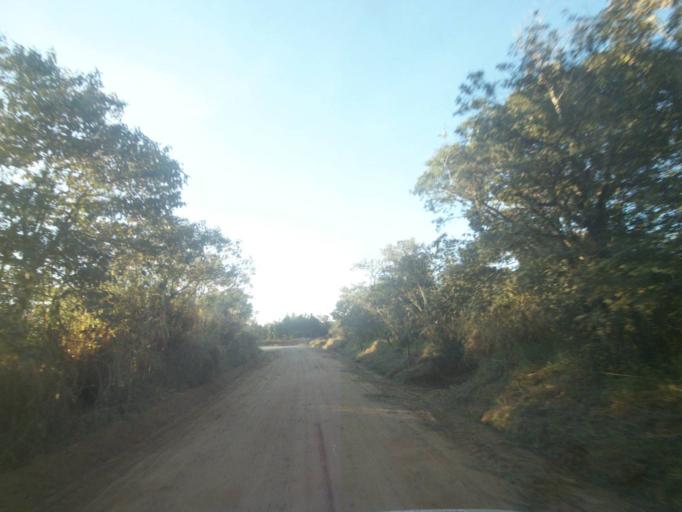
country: BR
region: Parana
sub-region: Tibagi
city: Tibagi
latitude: -24.5437
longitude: -50.5323
